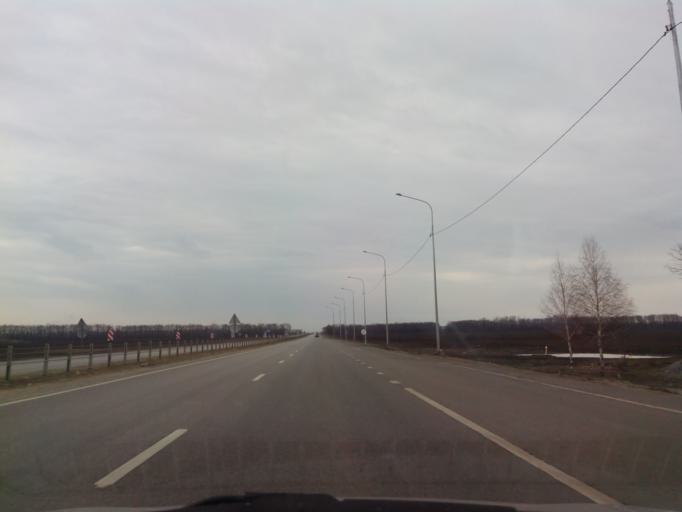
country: RU
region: Tambov
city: Zavoronezhskoye
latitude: 52.8920
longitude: 40.6942
